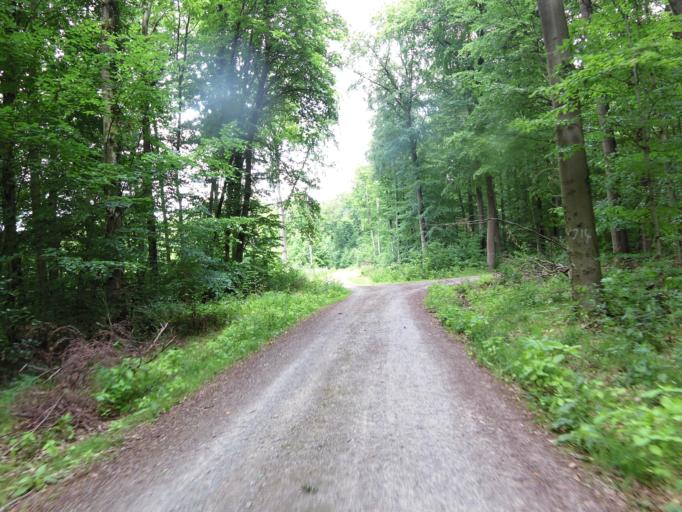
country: DE
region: Bavaria
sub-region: Regierungsbezirk Unterfranken
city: Wuerzburg
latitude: 49.7526
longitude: 9.8889
